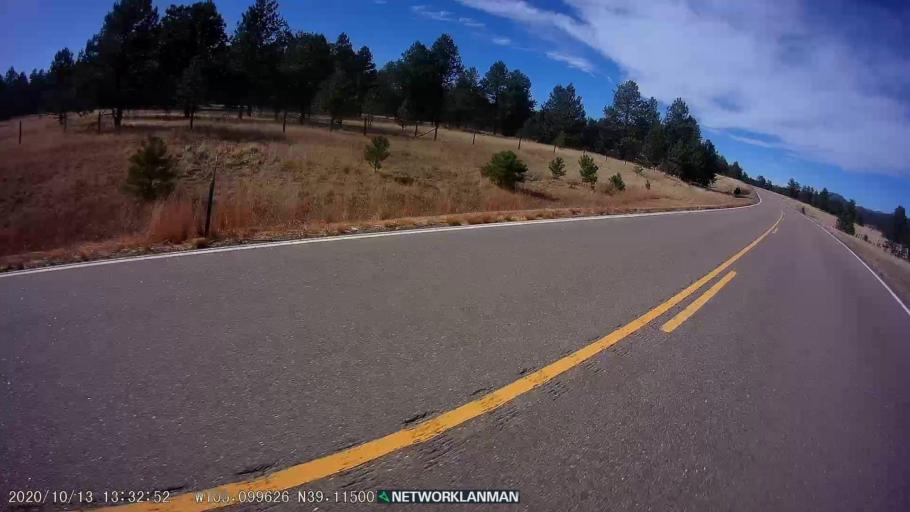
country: US
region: Colorado
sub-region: Teller County
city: Woodland Park
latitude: 39.1150
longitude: -105.0995
